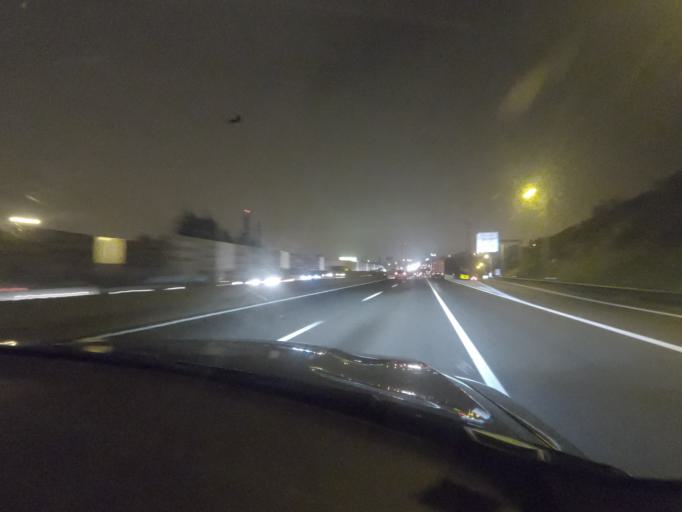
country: PT
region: Lisbon
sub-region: Loures
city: Santa Iria da Azoia
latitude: 38.8512
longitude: -9.0871
